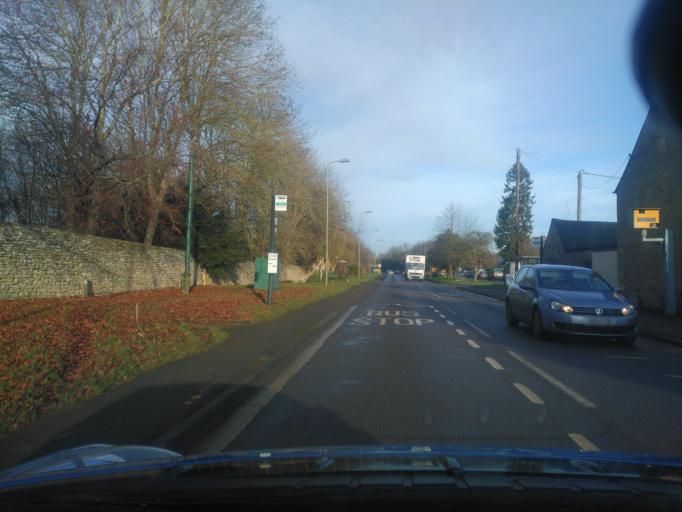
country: GB
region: England
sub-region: Oxfordshire
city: Woodstock
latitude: 51.8553
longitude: -1.3619
